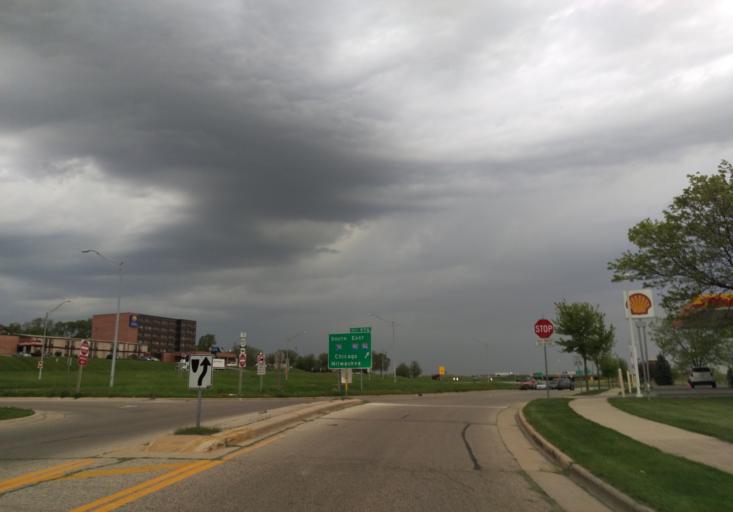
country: US
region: Wisconsin
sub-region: Dane County
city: Monona
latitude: 43.1328
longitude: -89.3005
